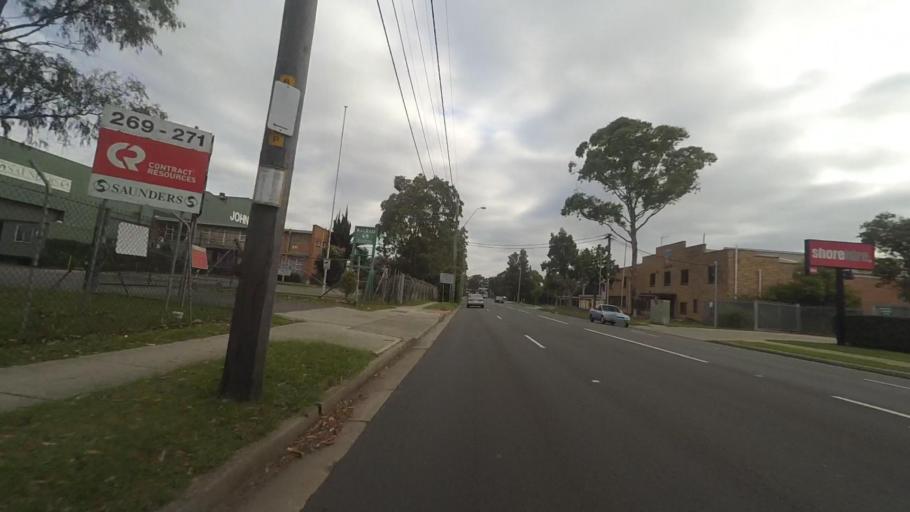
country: AU
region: New South Wales
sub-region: Bankstown
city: Revesby
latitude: -33.9334
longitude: 151.0118
